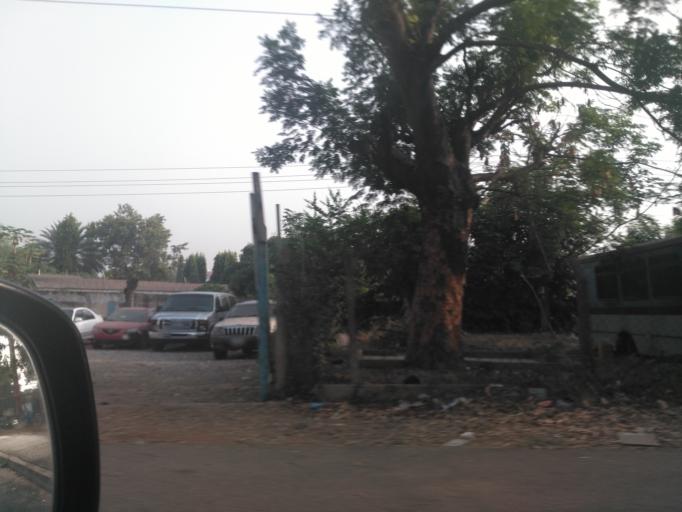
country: GH
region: Greater Accra
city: Accra
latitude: 5.6033
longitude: -0.2011
